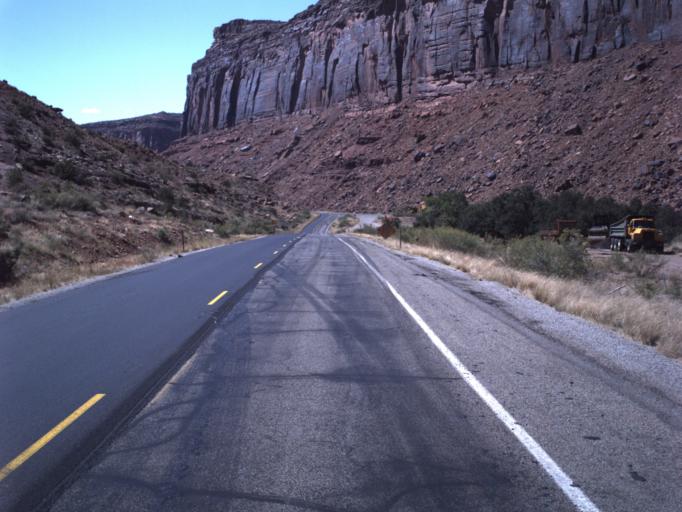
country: US
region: Utah
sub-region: Grand County
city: Moab
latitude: 38.6827
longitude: -109.4744
